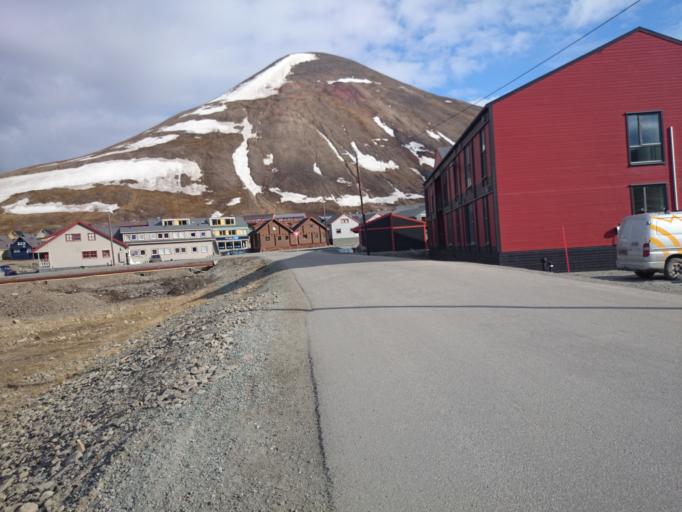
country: SJ
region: Svalbard
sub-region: Spitsbergen
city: Longyearbyen
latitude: 78.2185
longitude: 15.6324
